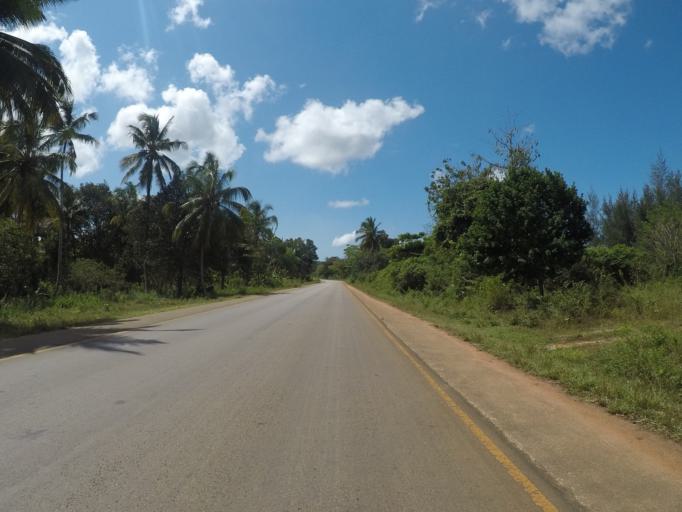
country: TZ
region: Zanzibar Central/South
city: Koani
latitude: -6.1716
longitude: 39.3298
